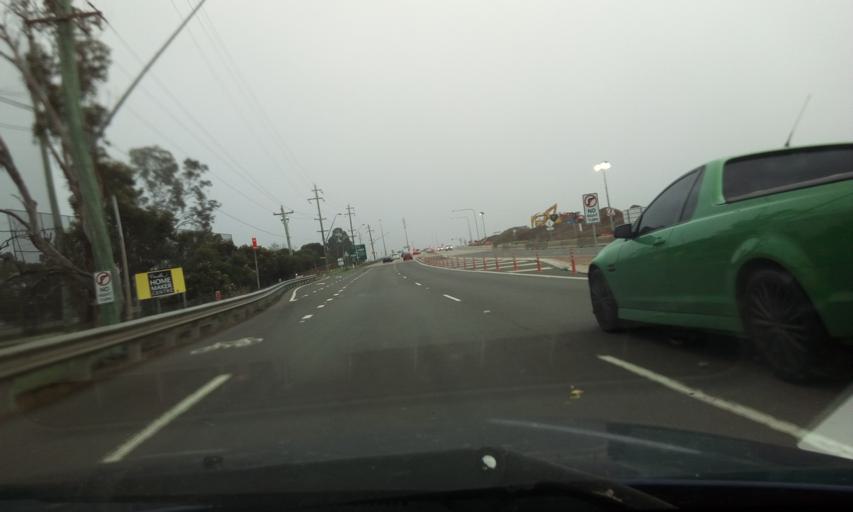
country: AU
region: New South Wales
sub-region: Penrith Municipality
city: Kingswood Park
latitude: -33.7888
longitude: 150.7008
